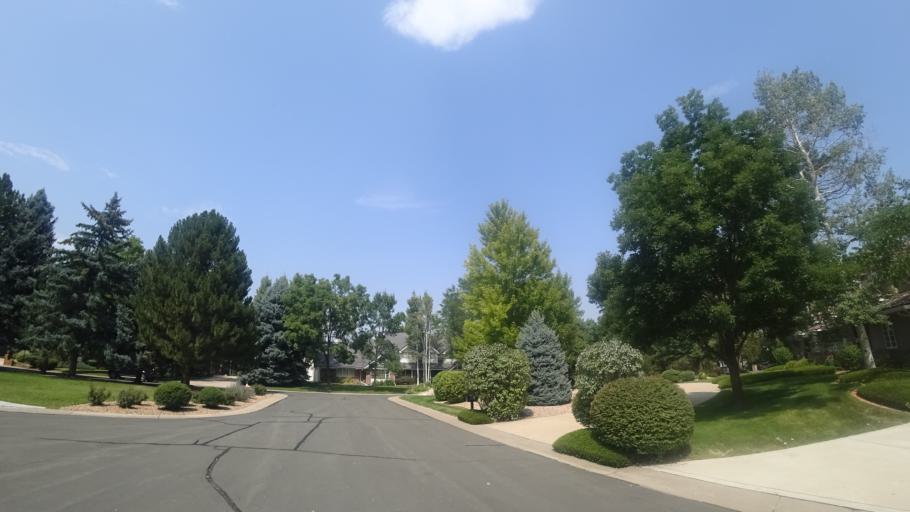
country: US
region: Colorado
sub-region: Arapahoe County
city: Greenwood Village
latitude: 39.6198
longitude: -104.9701
